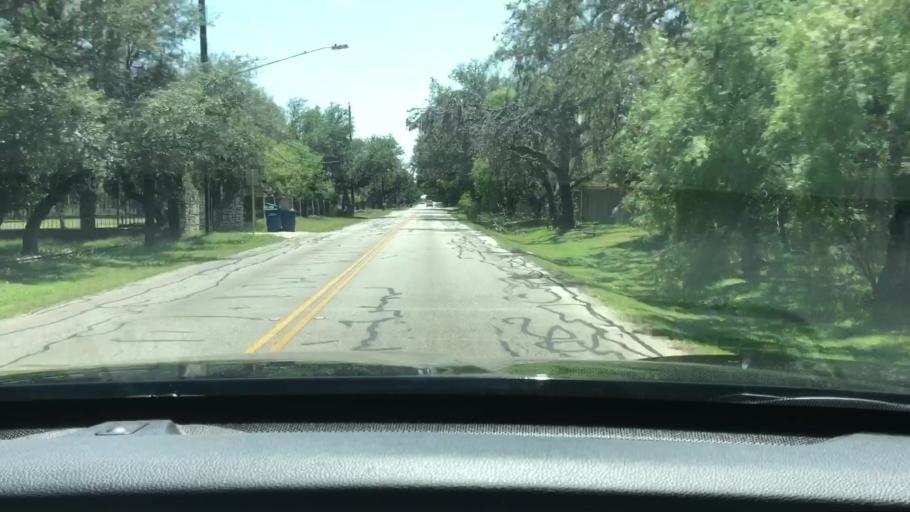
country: US
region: Texas
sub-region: Bexar County
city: Helotes
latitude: 29.5502
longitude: -98.6558
